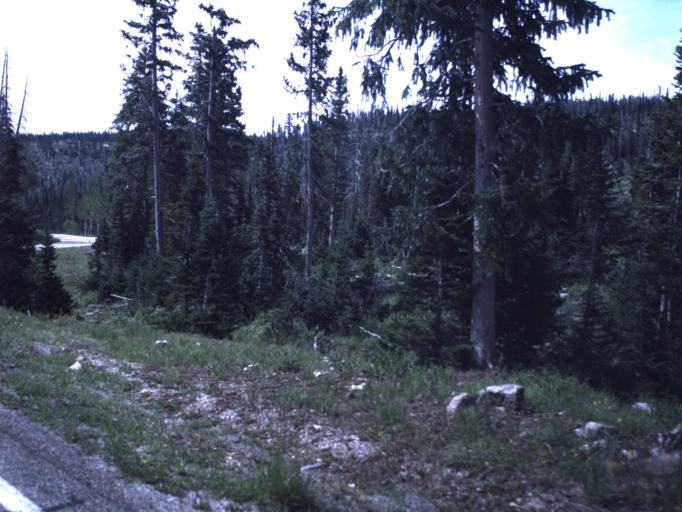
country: US
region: Utah
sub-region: Iron County
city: Cedar City
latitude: 37.5799
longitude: -112.8431
